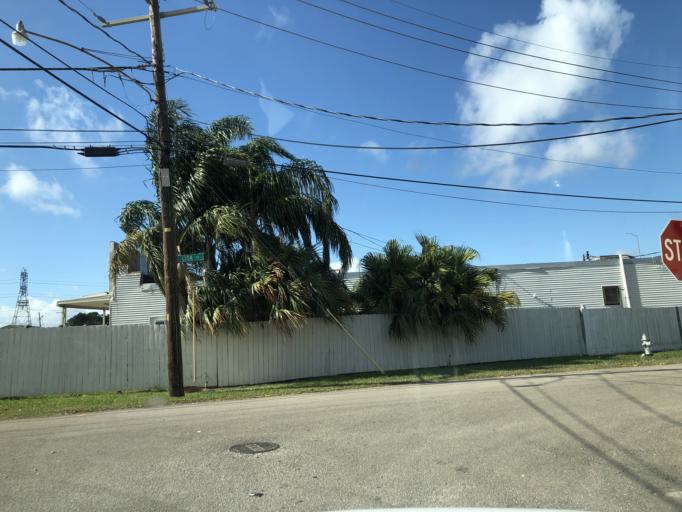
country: US
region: Louisiana
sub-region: Jefferson Parish
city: Kenner
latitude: 30.0068
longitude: -90.2193
